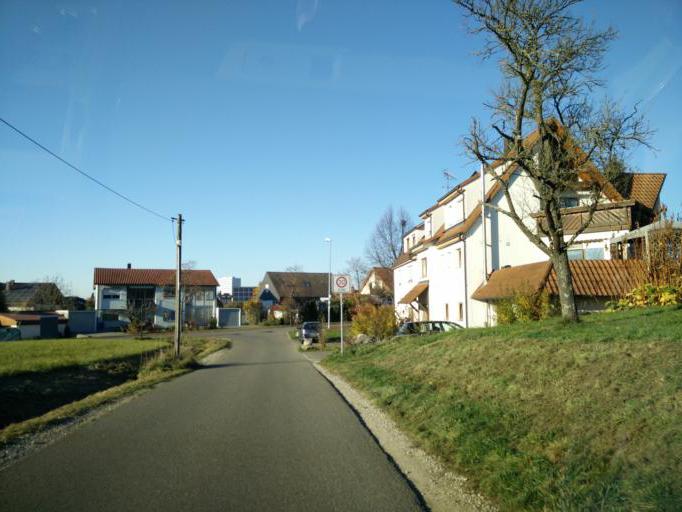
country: DE
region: Baden-Wuerttemberg
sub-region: Tuebingen Region
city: Gomaringen
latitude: 48.4480
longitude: 9.1032
